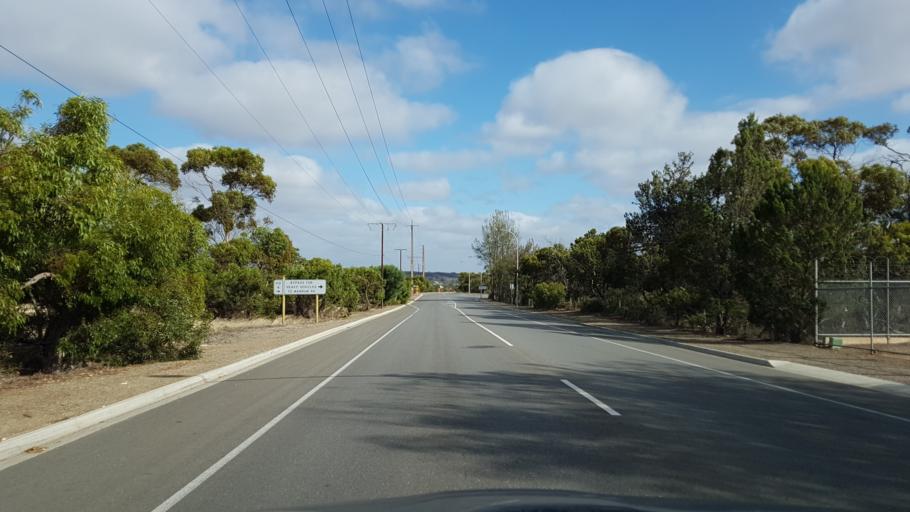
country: AU
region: South Australia
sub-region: Murray Bridge
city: Murray Bridge
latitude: -35.1182
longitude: 139.2483
